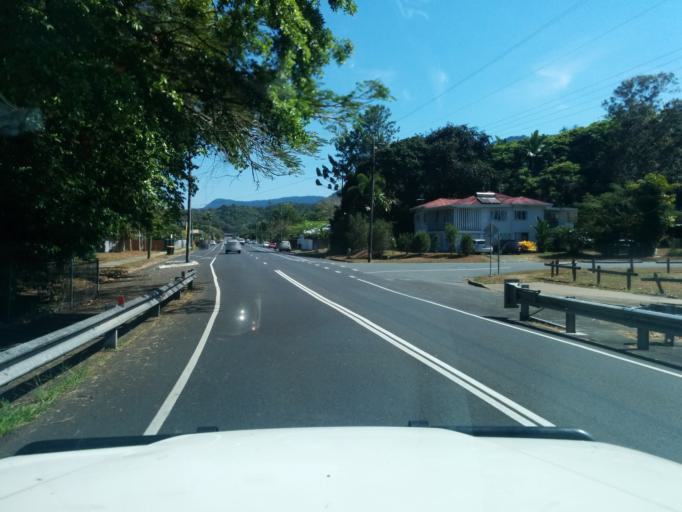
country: AU
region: Queensland
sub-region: Cairns
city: Redlynch
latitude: -16.9028
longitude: 145.7289
